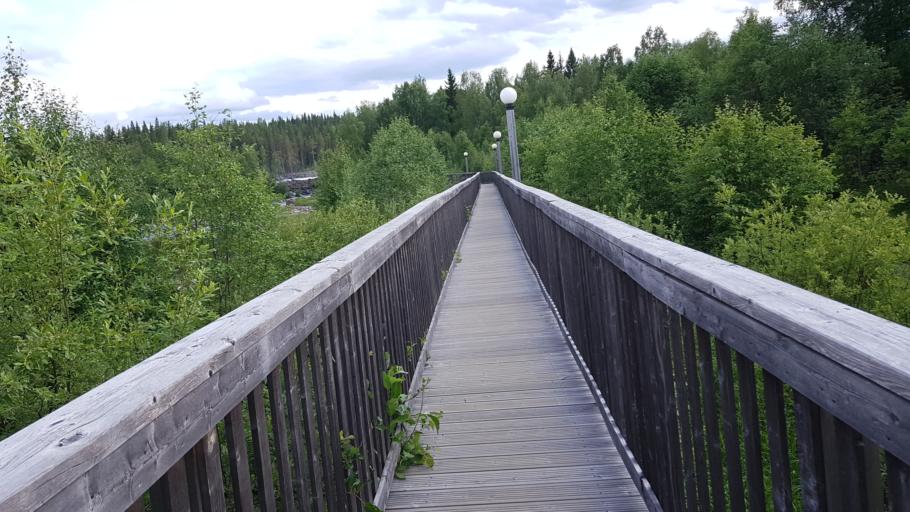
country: SE
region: Norrbotten
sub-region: Alvsbyns Kommun
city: AElvsbyn
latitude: 65.8558
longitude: 20.4163
